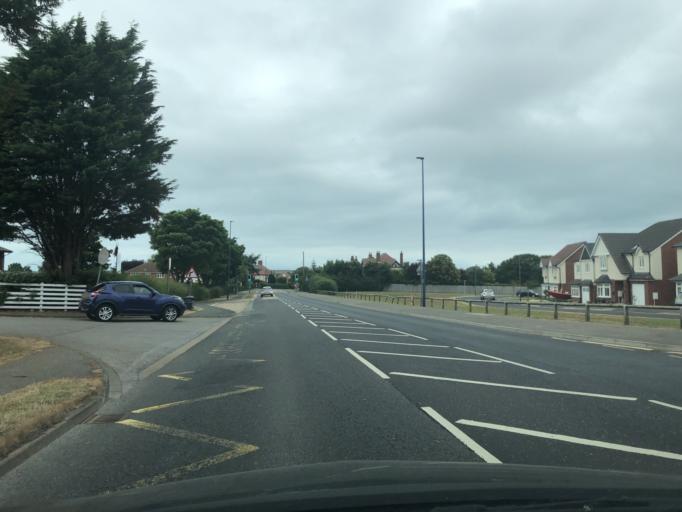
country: GB
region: England
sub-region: North Yorkshire
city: Filey
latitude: 54.2045
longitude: -0.3020
